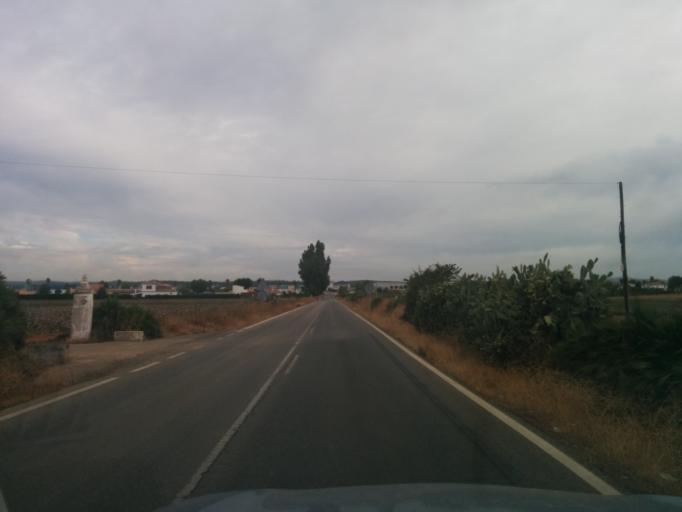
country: ES
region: Andalusia
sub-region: Provincia de Sevilla
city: Guillena
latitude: 37.5489
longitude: -6.0367
